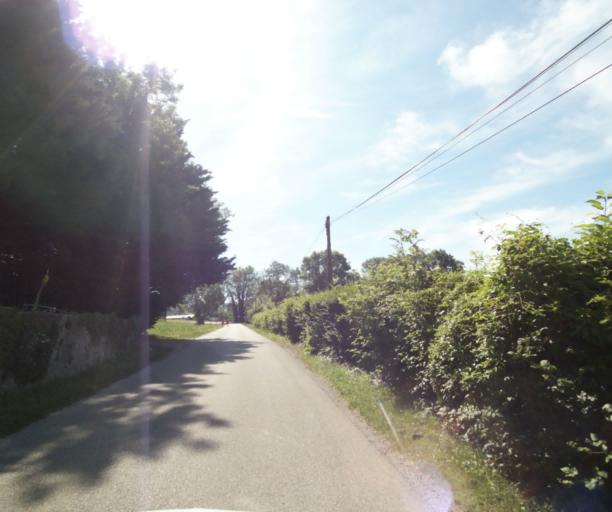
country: FR
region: Rhone-Alpes
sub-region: Departement de la Haute-Savoie
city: Anthy-sur-Leman
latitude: 46.3489
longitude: 6.4041
